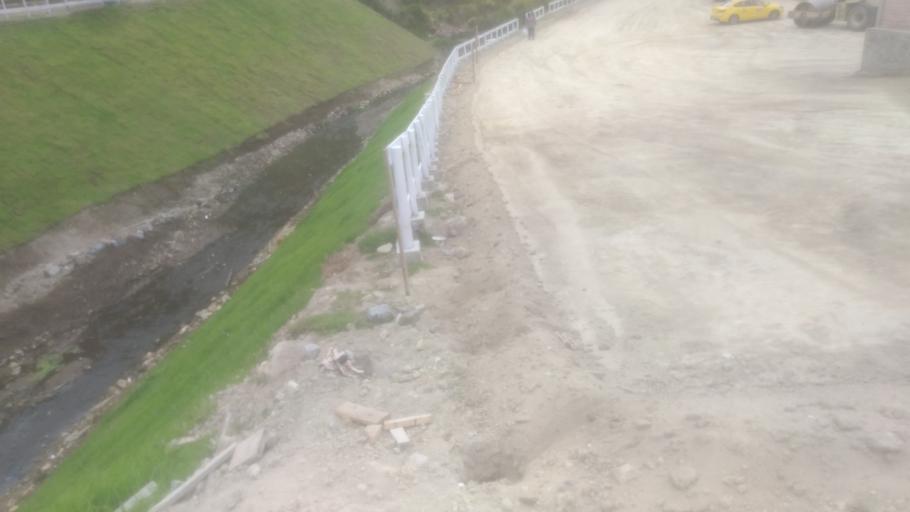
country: EC
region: Chimborazo
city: Riobamba
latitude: -1.7088
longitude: -78.7041
